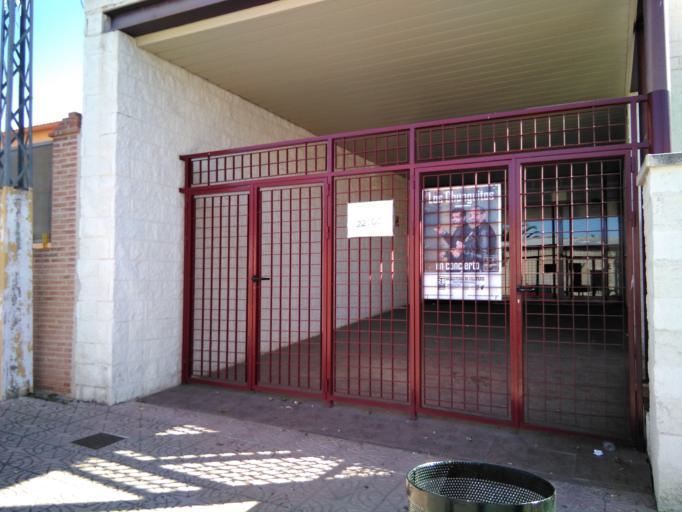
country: ES
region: Castille-La Mancha
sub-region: Provincia de Ciudad Real
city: Ballesteros de Calatrava
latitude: 38.8360
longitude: -3.9432
